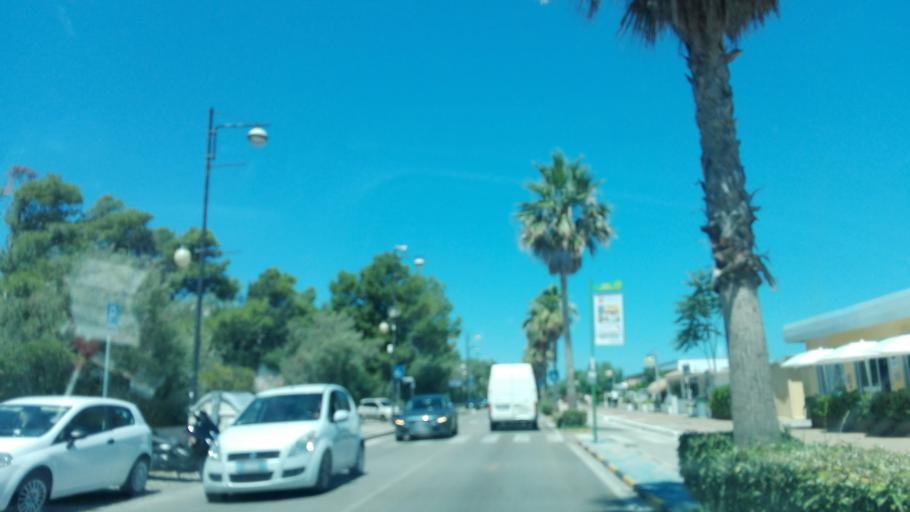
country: IT
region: Abruzzo
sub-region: Provincia di Pescara
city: Montesilvano Marina
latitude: 42.5029
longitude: 14.1758
